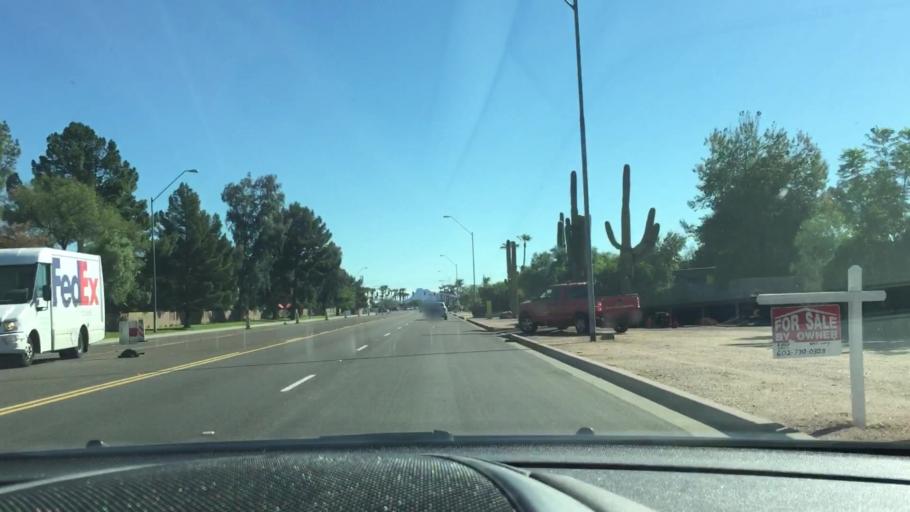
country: US
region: Arizona
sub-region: Maricopa County
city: Scottsdale
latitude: 33.5383
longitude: -111.8949
